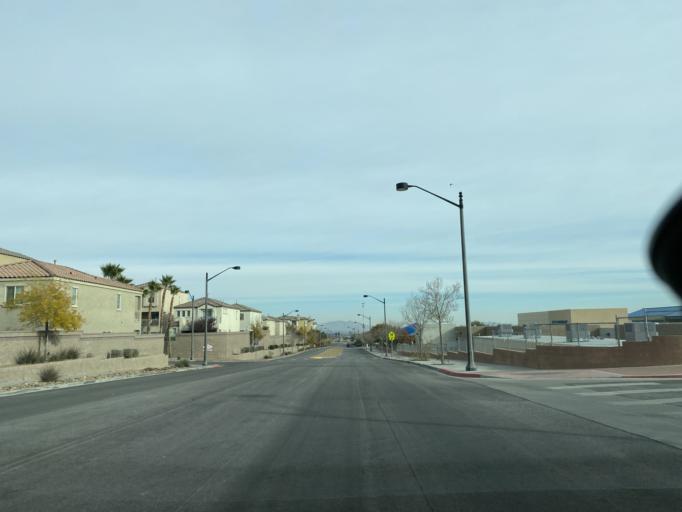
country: US
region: Nevada
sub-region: Clark County
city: Summerlin South
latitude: 36.2955
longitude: -115.2947
